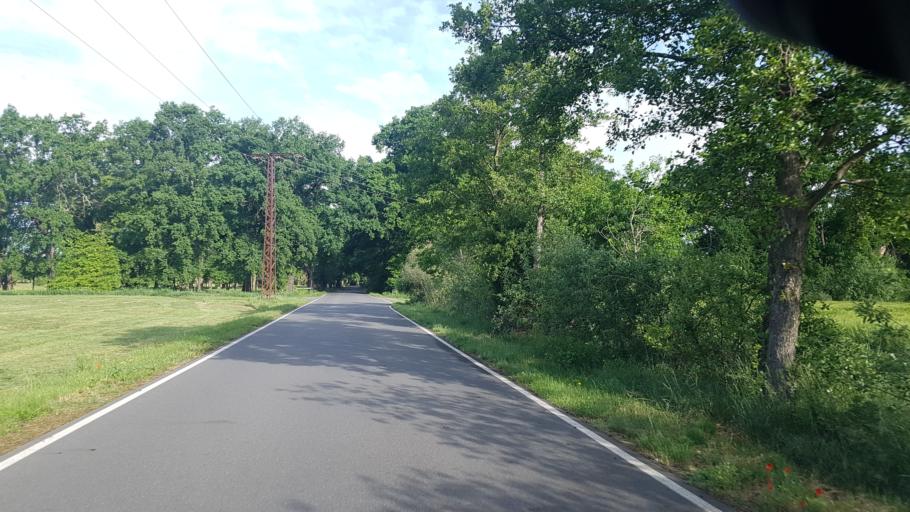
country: DE
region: Brandenburg
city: Luckau
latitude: 51.8278
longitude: 13.7496
